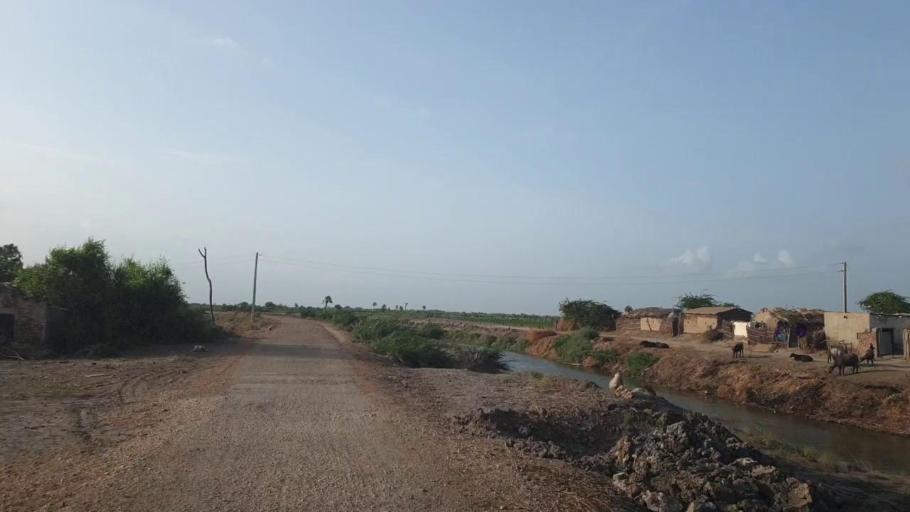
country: PK
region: Sindh
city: Kadhan
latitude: 24.6279
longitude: 69.1600
